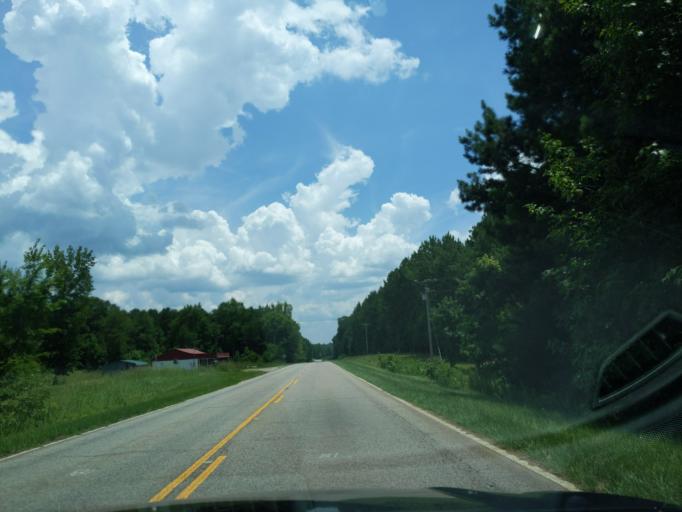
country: US
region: South Carolina
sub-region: Edgefield County
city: Edgefield
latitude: 33.8701
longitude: -81.9942
